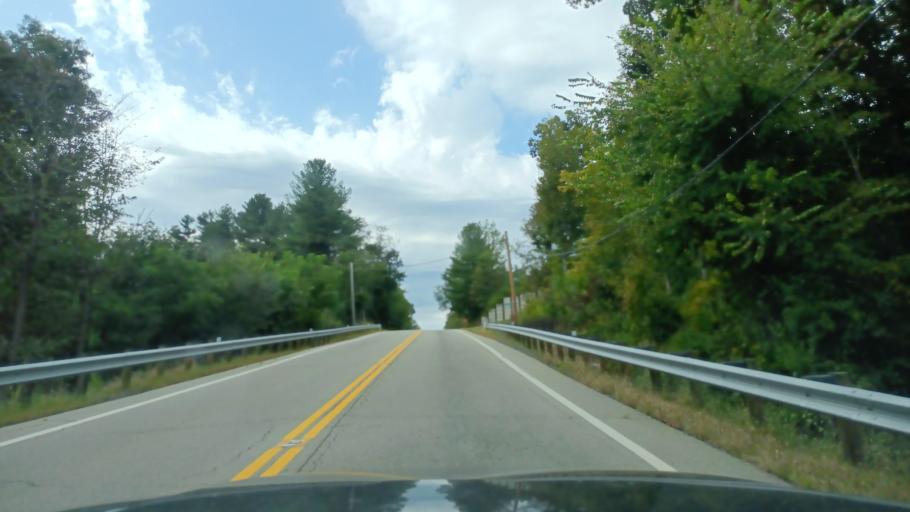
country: US
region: Ohio
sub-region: Vinton County
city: McArthur
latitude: 39.2366
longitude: -82.3413
